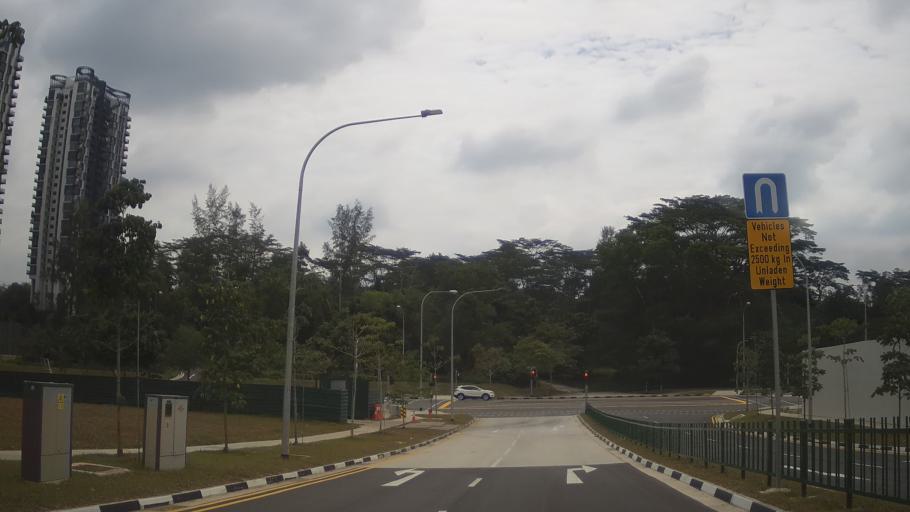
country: MY
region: Johor
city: Johor Bahru
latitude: 1.3672
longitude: 103.7747
